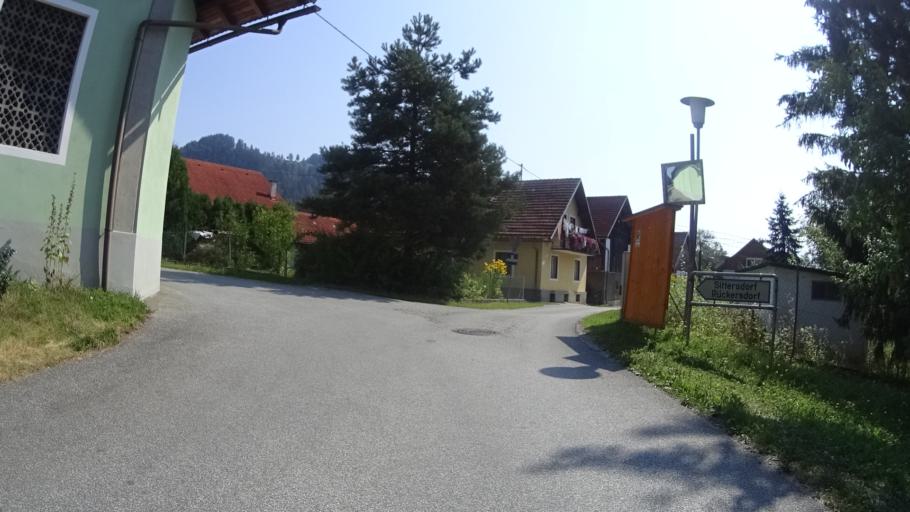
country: AT
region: Carinthia
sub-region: Politischer Bezirk Volkermarkt
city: Gallizien
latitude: 46.5703
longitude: 14.5154
